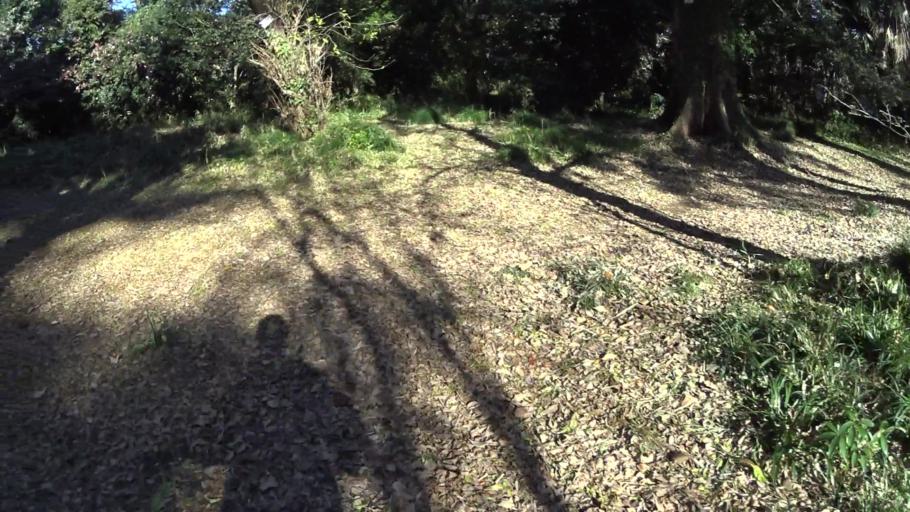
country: JP
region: Tokyo
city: Tokyo
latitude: 35.7220
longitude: 139.7426
